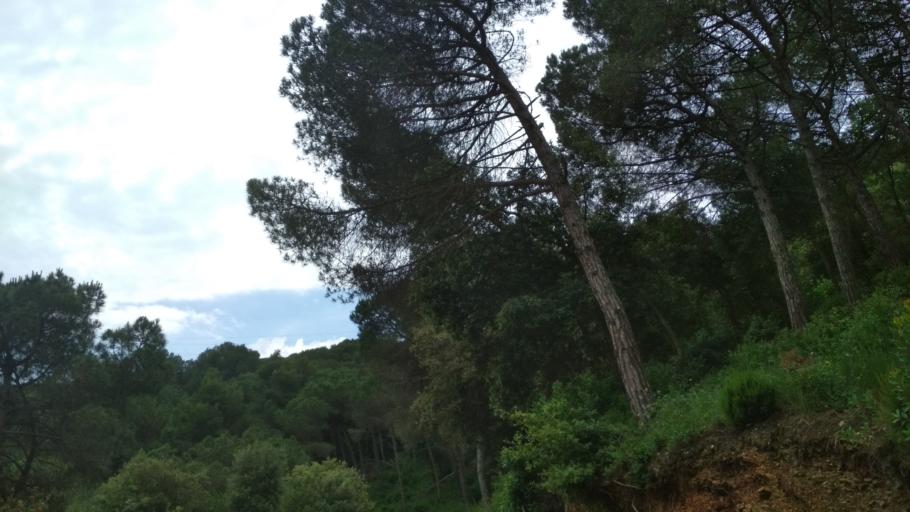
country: ES
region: Catalonia
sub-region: Provincia de Barcelona
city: Nou Barris
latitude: 41.4533
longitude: 2.1660
